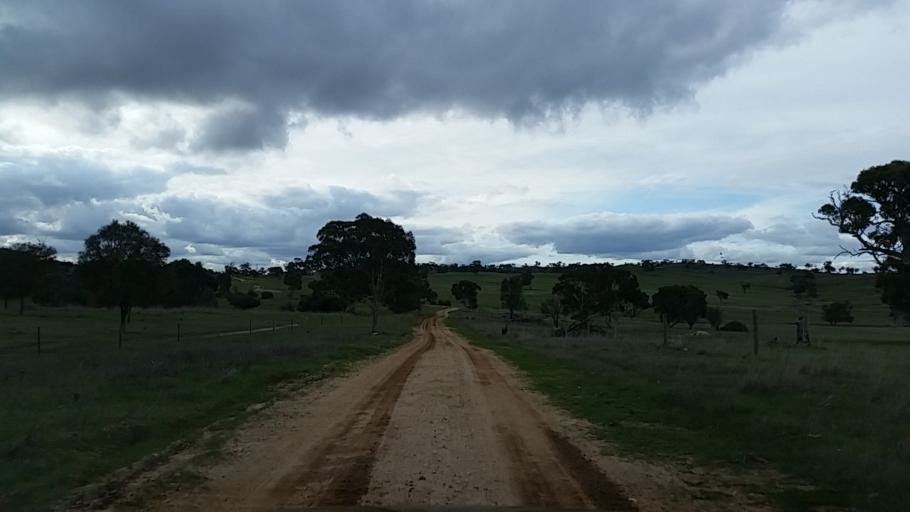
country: AU
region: South Australia
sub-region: Mount Barker
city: Callington
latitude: -34.9669
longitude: 139.0541
